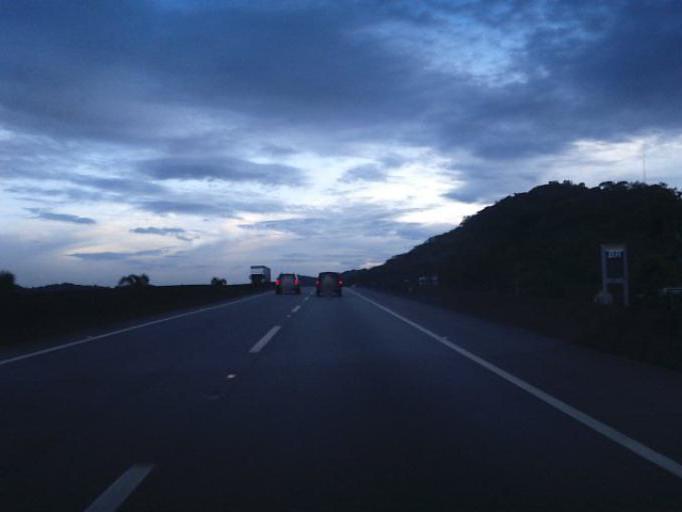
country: BR
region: Santa Catarina
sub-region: Joinville
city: Joinville
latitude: -26.2021
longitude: -48.9135
